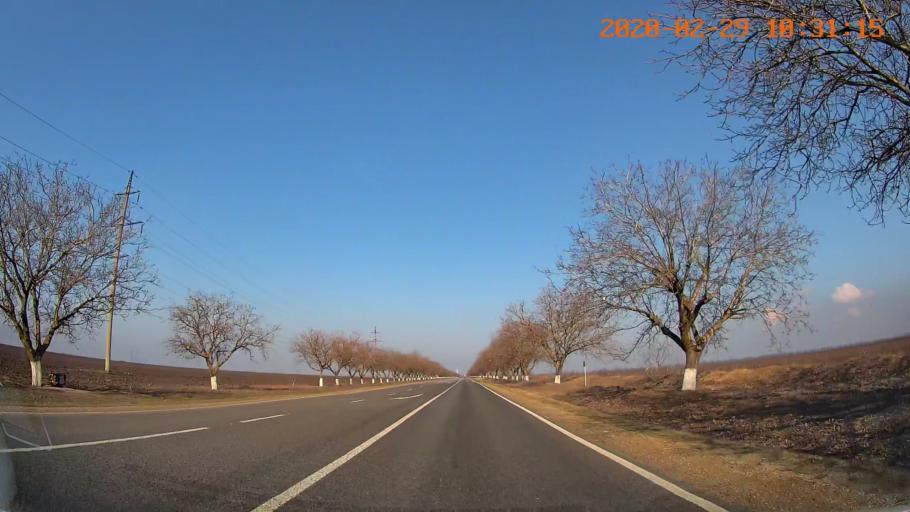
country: MD
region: Telenesti
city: Tiraspolul Nou
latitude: 46.9458
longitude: 29.5663
